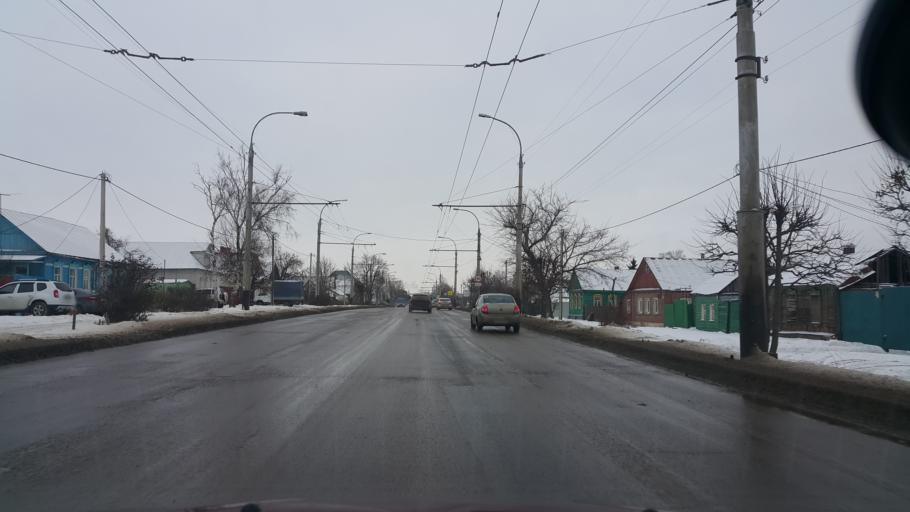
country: RU
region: Tambov
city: Tambov
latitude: 52.7248
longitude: 41.4034
